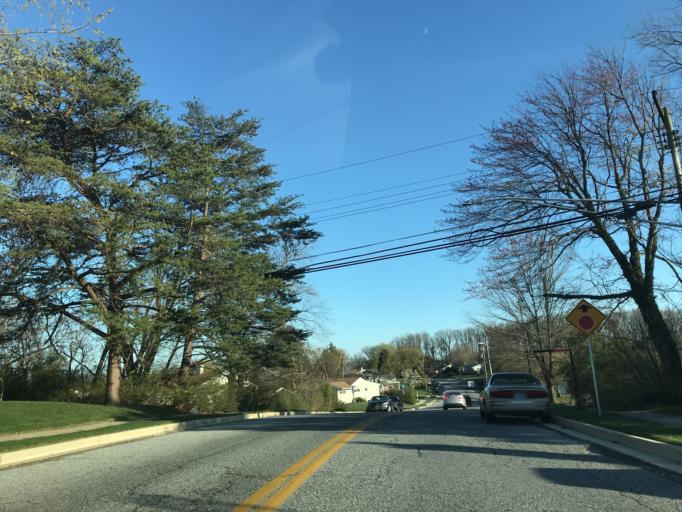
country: US
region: Maryland
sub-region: Baltimore County
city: Carney
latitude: 39.3949
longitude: -76.5354
